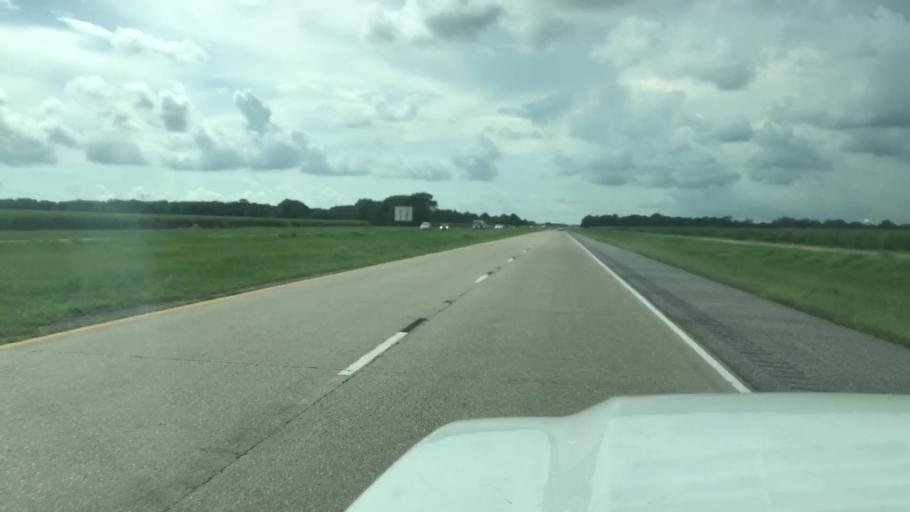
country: US
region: Louisiana
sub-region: Saint Mary Parish
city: Franklin
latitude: 29.7594
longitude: -91.4758
